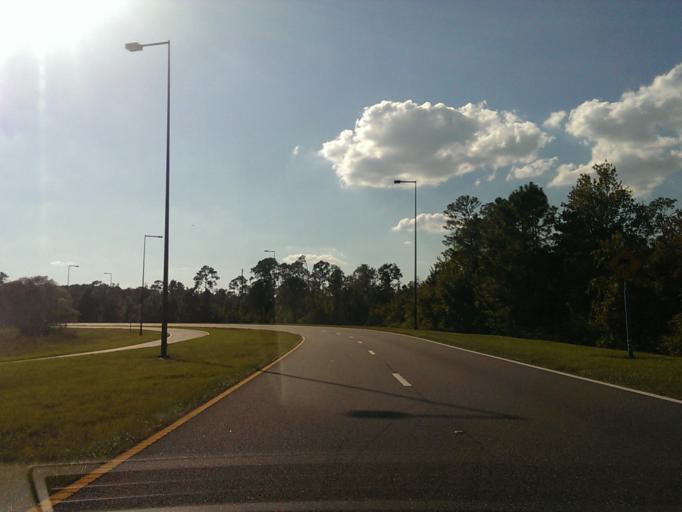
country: US
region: Florida
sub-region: Osceola County
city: Celebration
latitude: 28.3824
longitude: -81.5586
